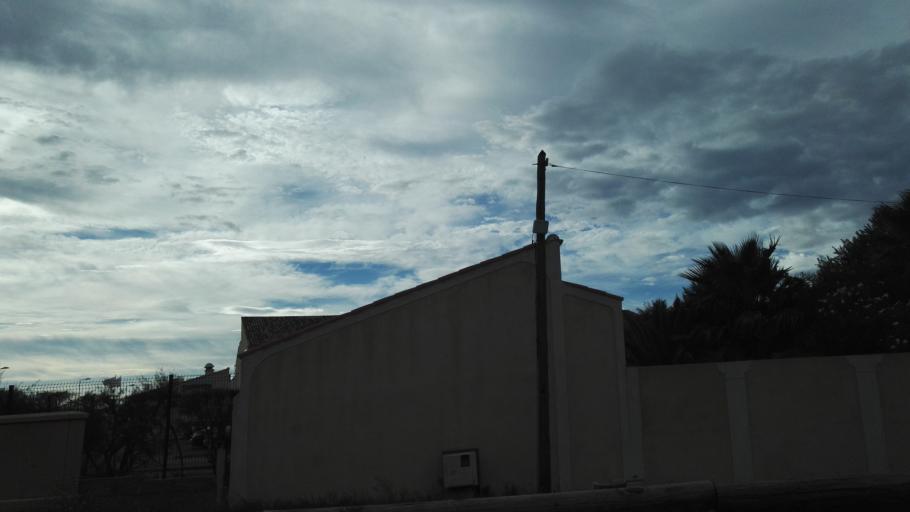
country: FR
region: Languedoc-Roussillon
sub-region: Departement de l'Herault
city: Marseillan
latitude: 43.3224
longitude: 3.5555
